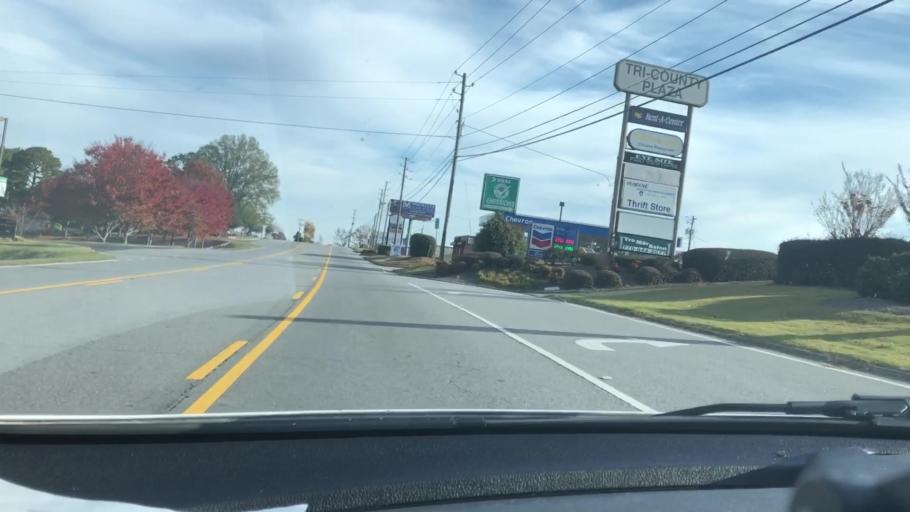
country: US
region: Georgia
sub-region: Forsyth County
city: Cumming
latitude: 34.1894
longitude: -84.1382
